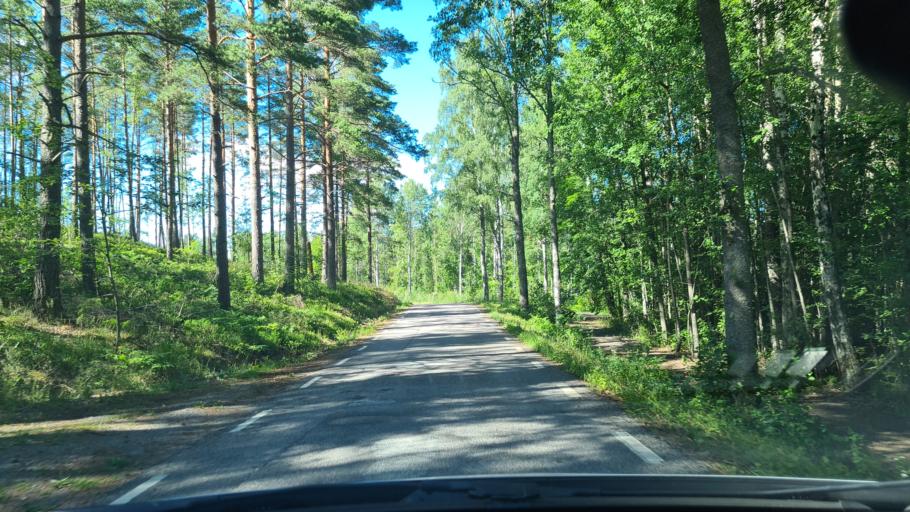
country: SE
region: OEstergoetland
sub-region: Norrkopings Kommun
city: Krokek
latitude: 58.7217
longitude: 16.4305
